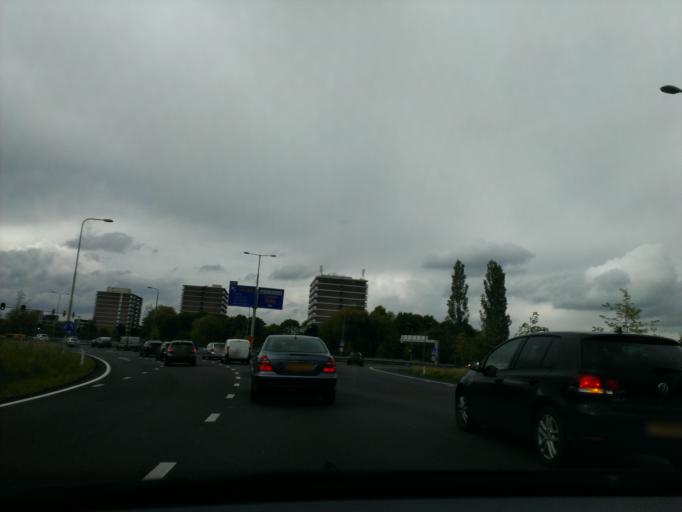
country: NL
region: Gelderland
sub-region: Gemeente Rheden
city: Velp
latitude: 51.9818
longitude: 5.9809
